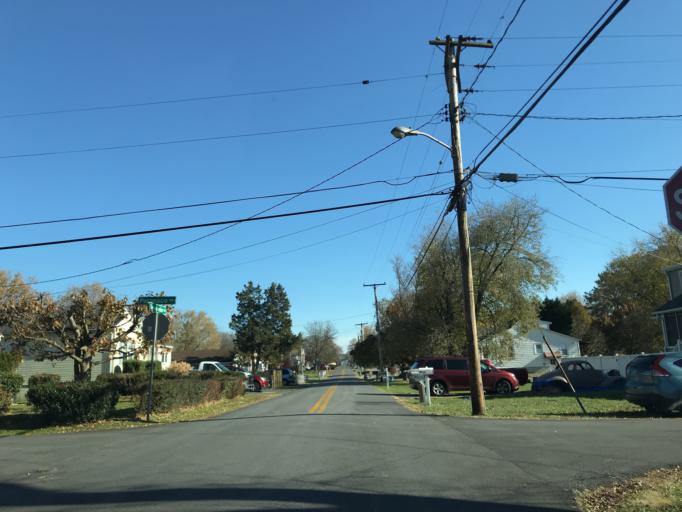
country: US
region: Maryland
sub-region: Baltimore County
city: Bowleys Quarters
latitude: 39.3732
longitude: -76.3450
